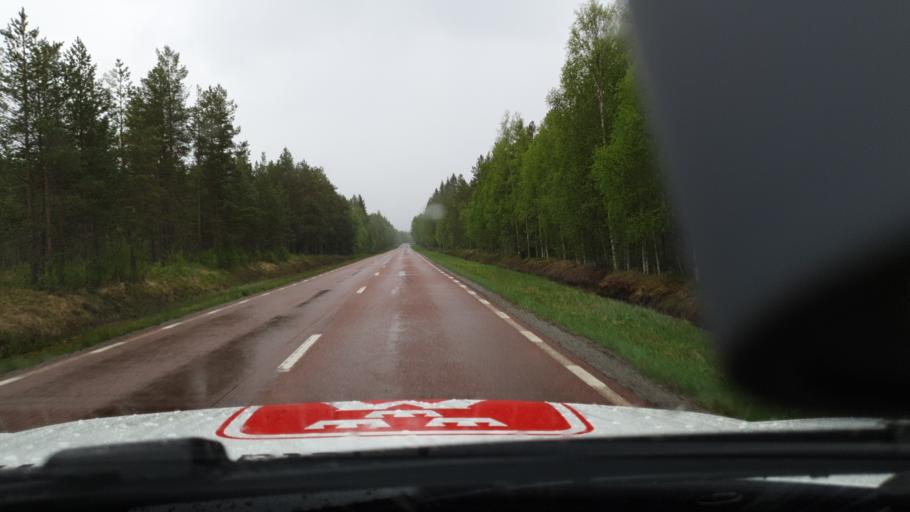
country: SE
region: Vaesterbotten
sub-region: Dorotea Kommun
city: Dorotea
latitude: 64.0881
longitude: 16.0860
